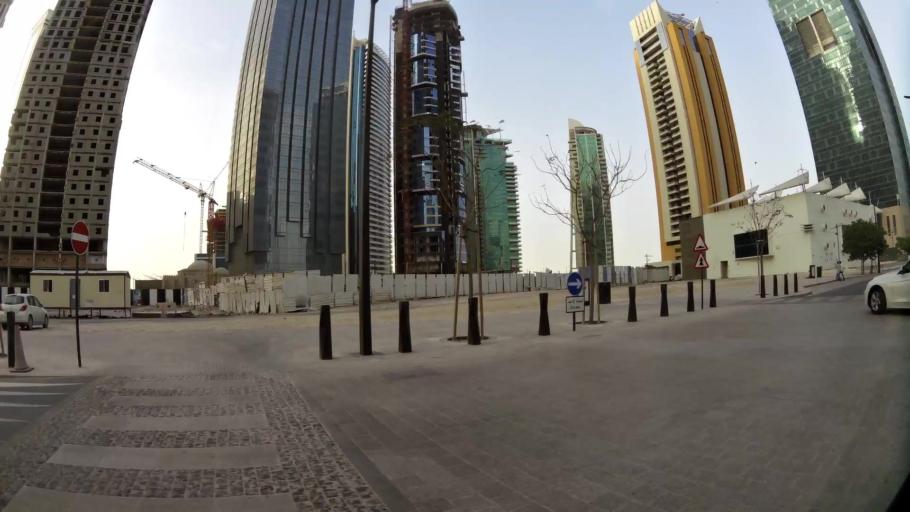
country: QA
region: Baladiyat ad Dawhah
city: Doha
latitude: 25.3276
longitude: 51.5351
